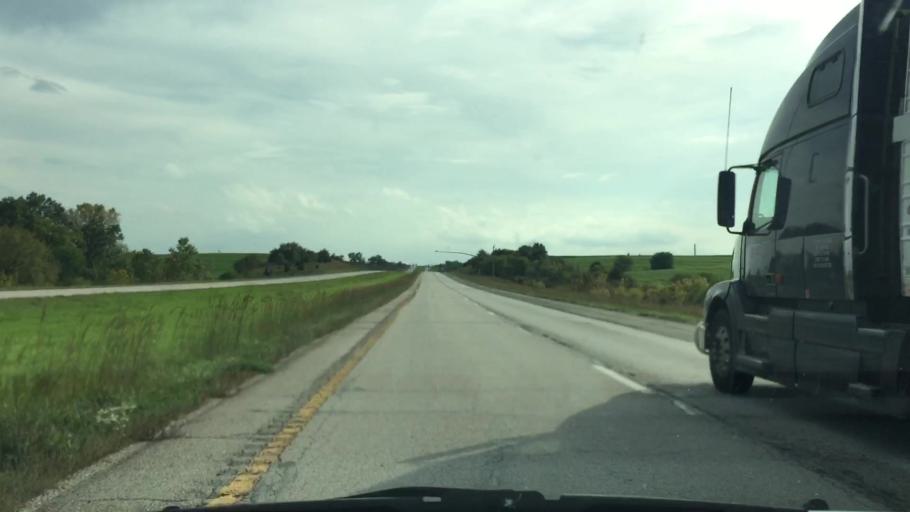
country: US
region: Iowa
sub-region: Decatur County
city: Lamoni
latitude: 40.5431
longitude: -93.9554
